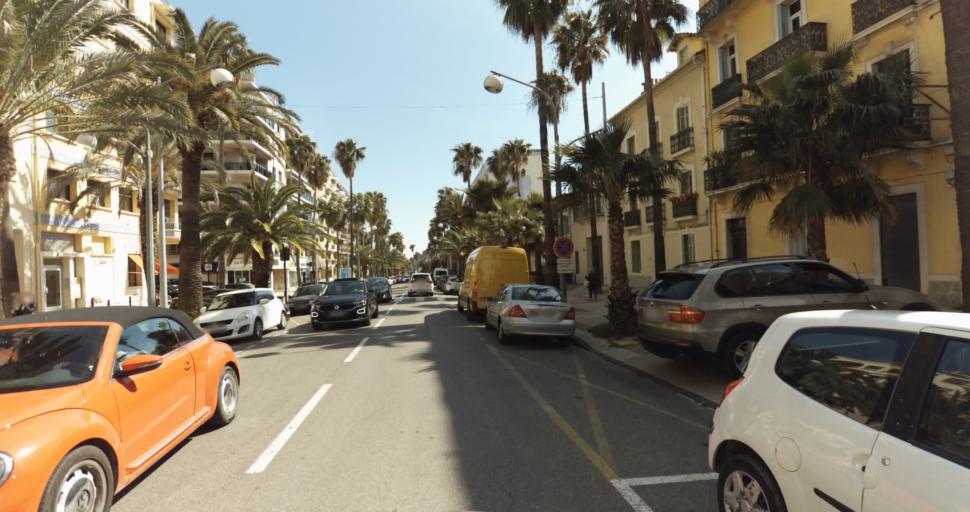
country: FR
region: Provence-Alpes-Cote d'Azur
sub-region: Departement du Var
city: Hyeres
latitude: 43.1160
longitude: 6.1286
